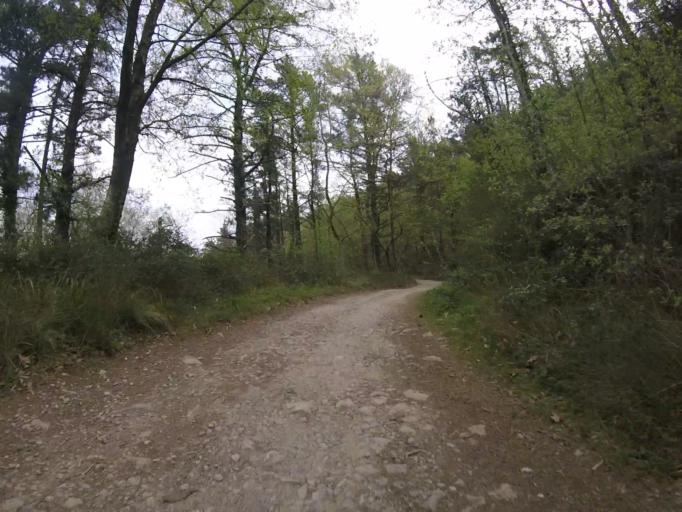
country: ES
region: Basque Country
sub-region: Provincia de Guipuzcoa
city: Usurbil
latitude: 43.2548
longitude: -2.0823
